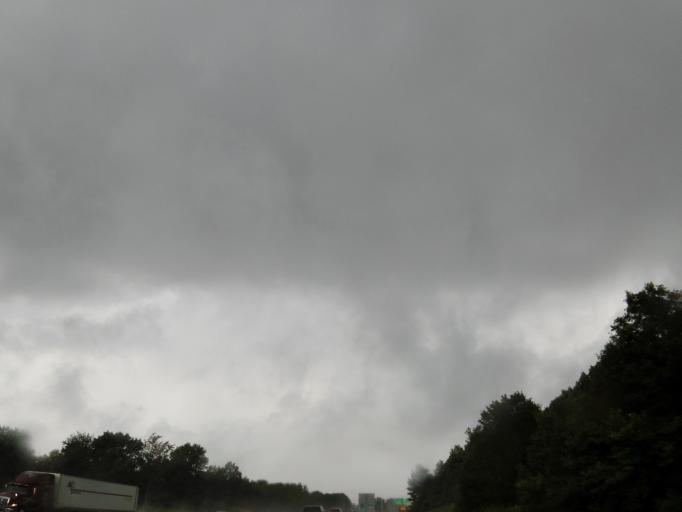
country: US
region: Illinois
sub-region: Jefferson County
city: Mount Vernon
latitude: 38.2599
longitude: -88.9253
